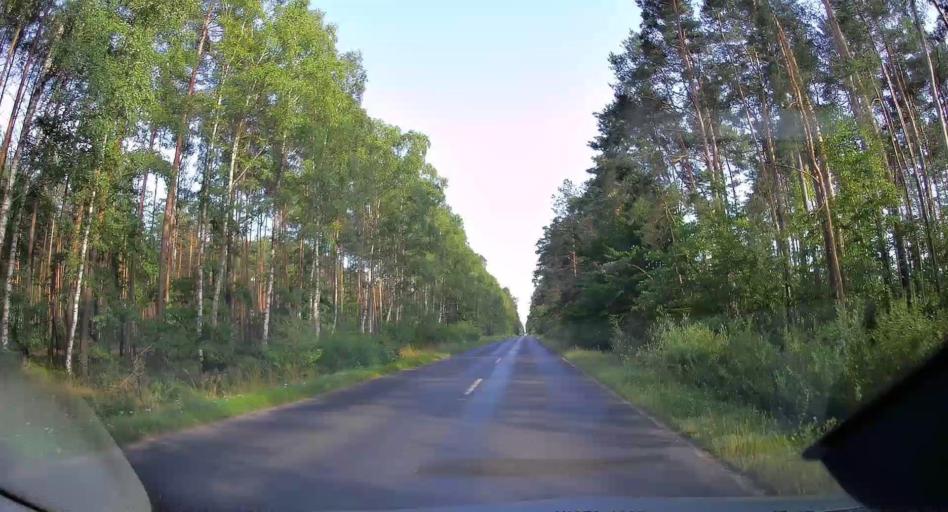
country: PL
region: Swietokrzyskie
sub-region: Powiat konecki
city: Smykow
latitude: 51.1078
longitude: 20.3506
